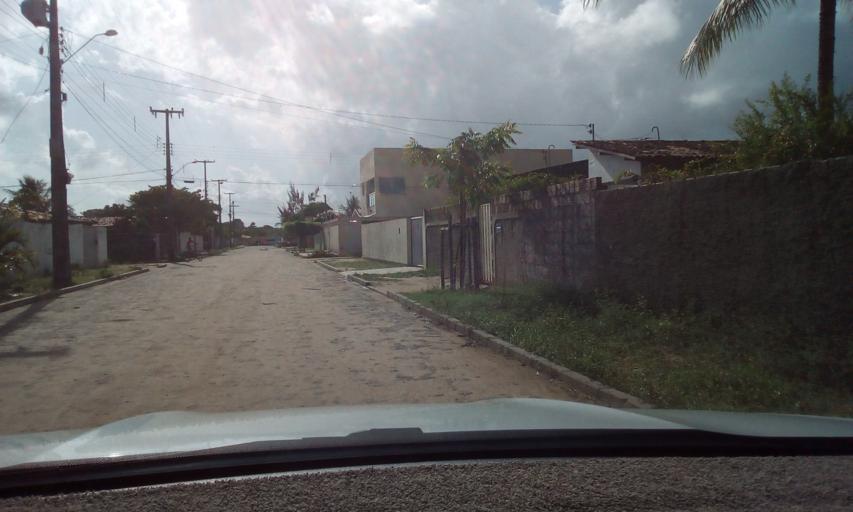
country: BR
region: Paraiba
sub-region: Joao Pessoa
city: Joao Pessoa
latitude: -7.1839
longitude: -34.8246
